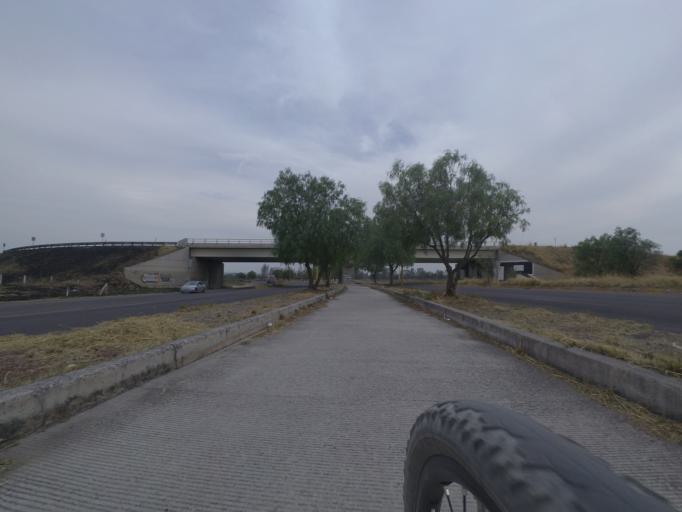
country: MX
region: Aguascalientes
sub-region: Aguascalientes
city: La Loma de los Negritos
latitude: 21.8638
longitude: -102.3714
